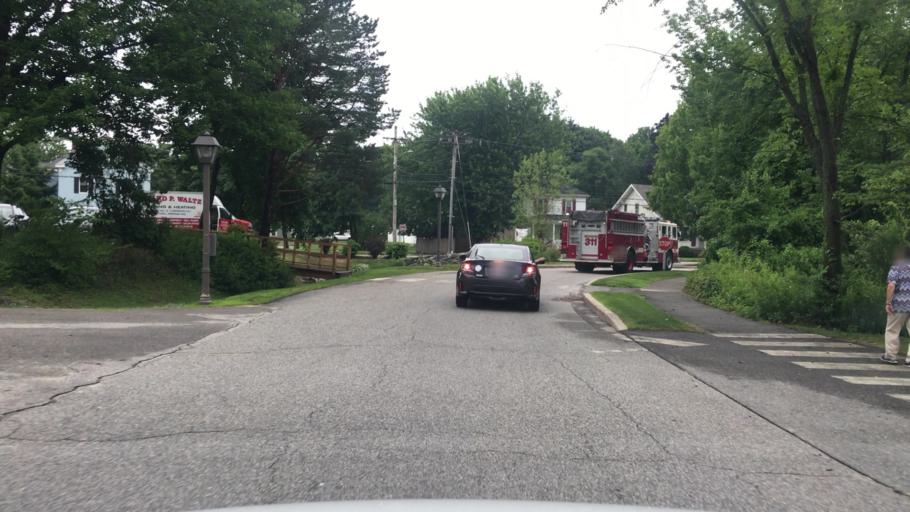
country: US
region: Maine
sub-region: Cumberland County
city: Portland
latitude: 43.6888
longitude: -70.2671
